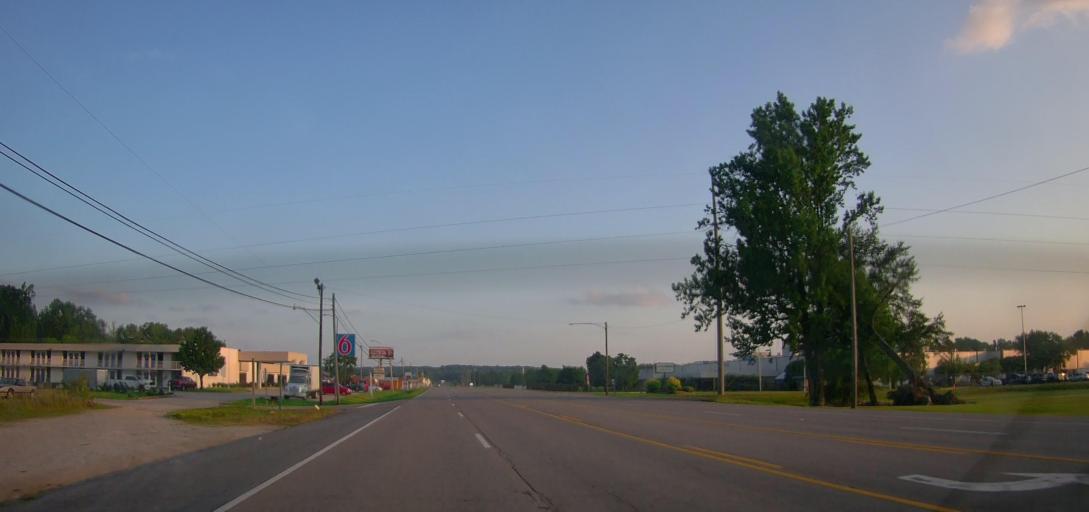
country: US
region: Alabama
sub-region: Marion County
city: Hamilton
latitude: 34.1156
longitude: -87.9894
